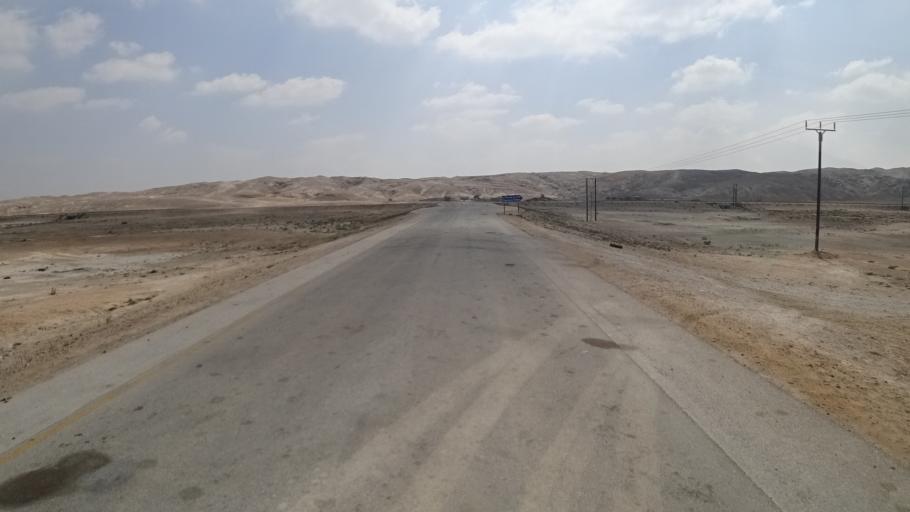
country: OM
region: Zufar
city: Salalah
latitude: 17.2404
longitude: 53.9164
